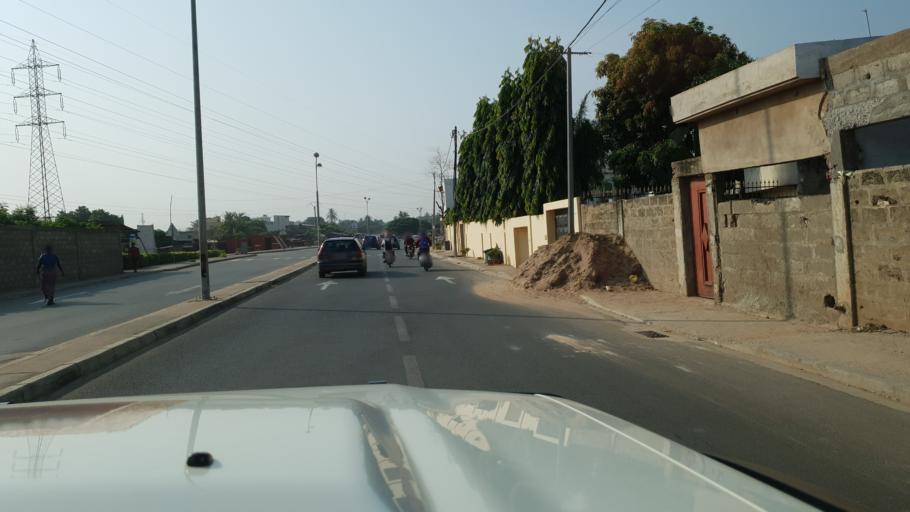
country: TG
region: Maritime
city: Lome
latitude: 6.1848
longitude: 1.2030
